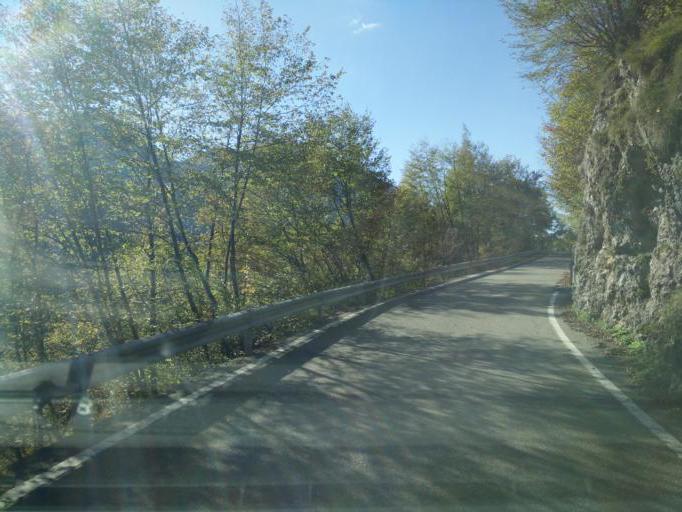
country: IT
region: Lombardy
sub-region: Provincia di Brescia
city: Capovalle
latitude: 45.7508
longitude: 10.5646
